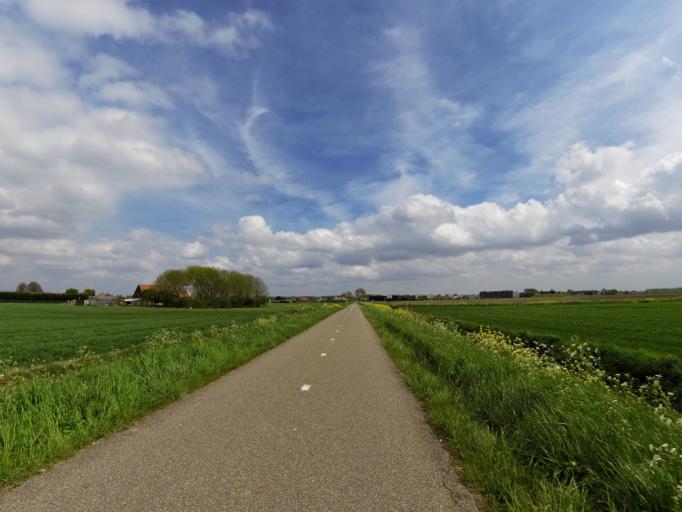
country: NL
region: South Holland
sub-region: Gemeente Spijkenisse
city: Spijkenisse
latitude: 51.8254
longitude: 4.2369
